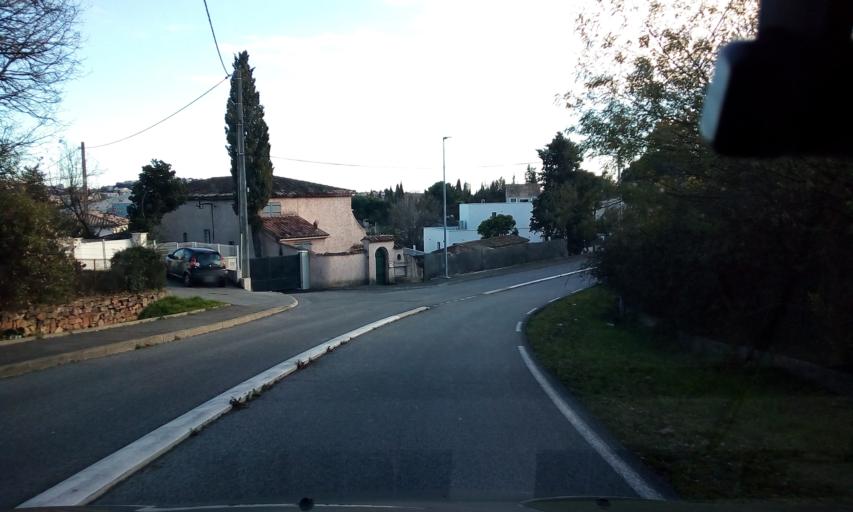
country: FR
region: Provence-Alpes-Cote d'Azur
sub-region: Departement du Var
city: Saint-Raphael
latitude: 43.4401
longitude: 6.7673
